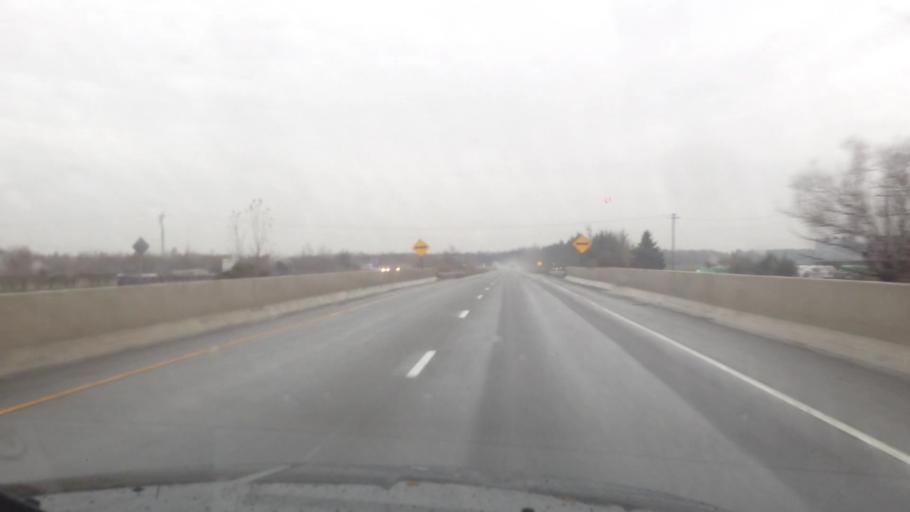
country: CA
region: Ontario
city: Casselman
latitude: 45.3105
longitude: -75.1524
